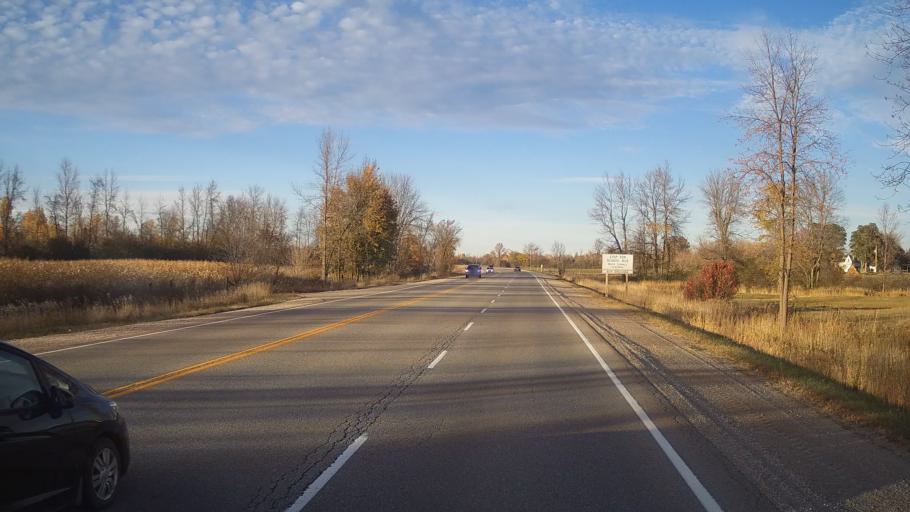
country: CA
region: Ontario
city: Perth
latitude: 44.9743
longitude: -76.2275
